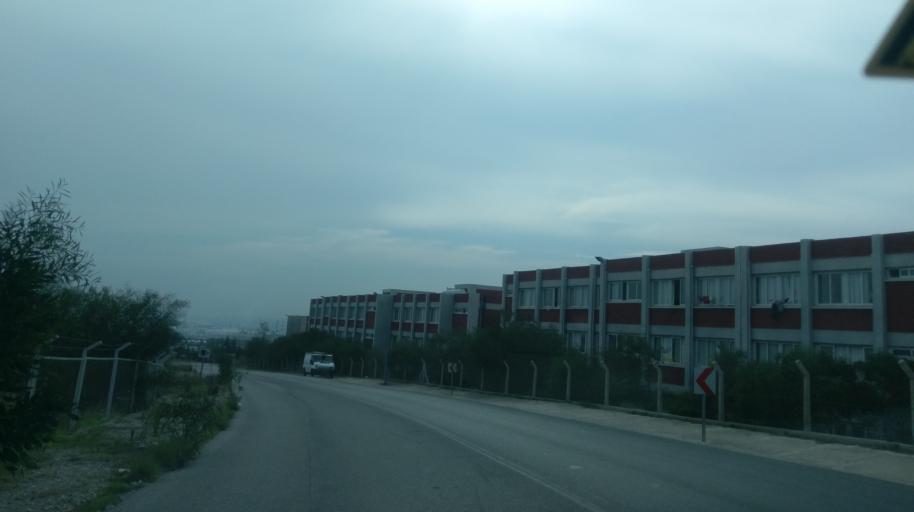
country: CY
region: Lefkosia
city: Nicosia
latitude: 35.2306
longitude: 33.3258
